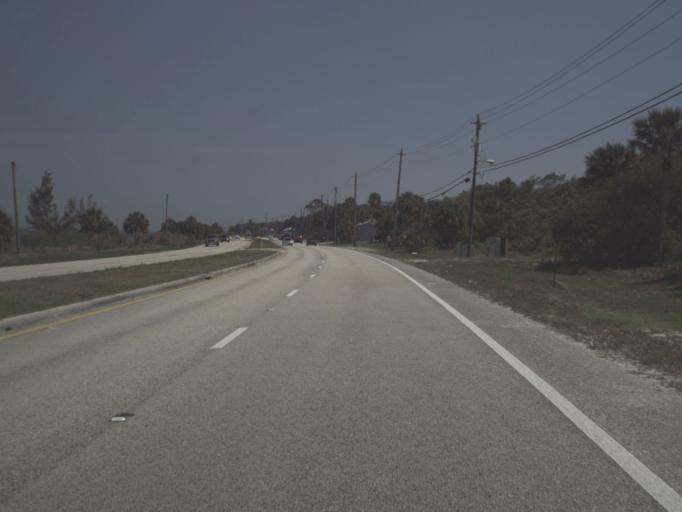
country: US
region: Florida
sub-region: Brevard County
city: Malabar
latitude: 28.0097
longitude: -80.5670
